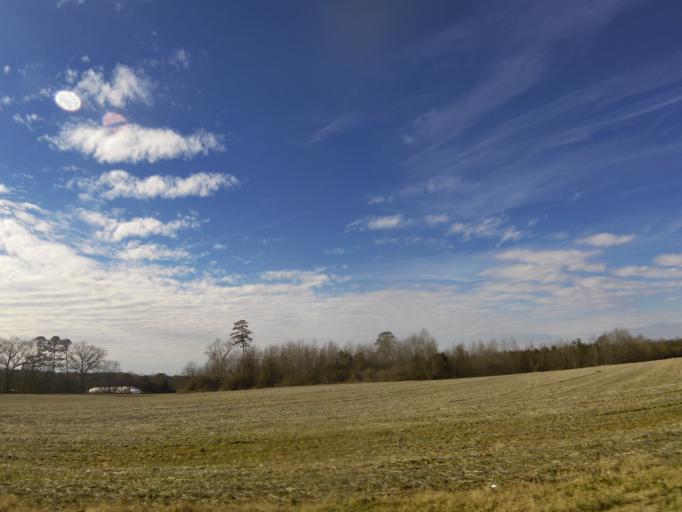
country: US
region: Virginia
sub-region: City of Franklin
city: Franklin
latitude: 36.7671
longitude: -76.8560
